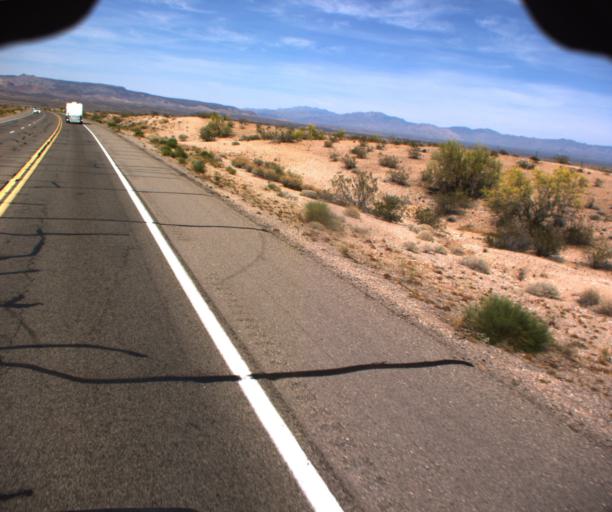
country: US
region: Arizona
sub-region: Mohave County
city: Desert Hills
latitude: 34.6851
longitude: -114.3038
